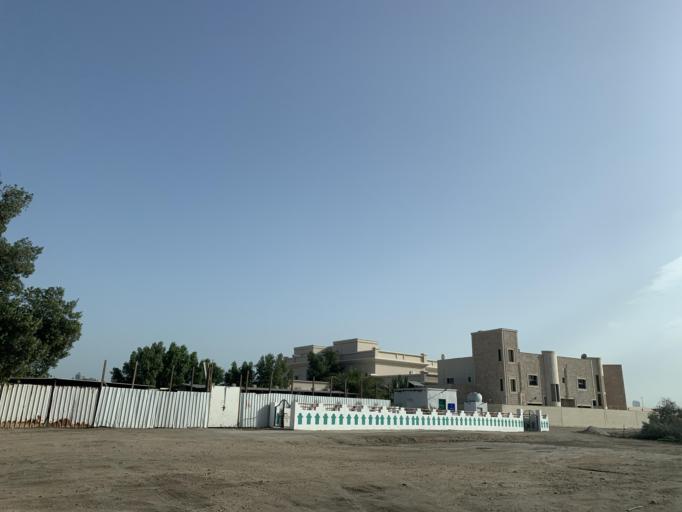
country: BH
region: Manama
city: Manama
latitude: 26.1843
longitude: 50.5861
